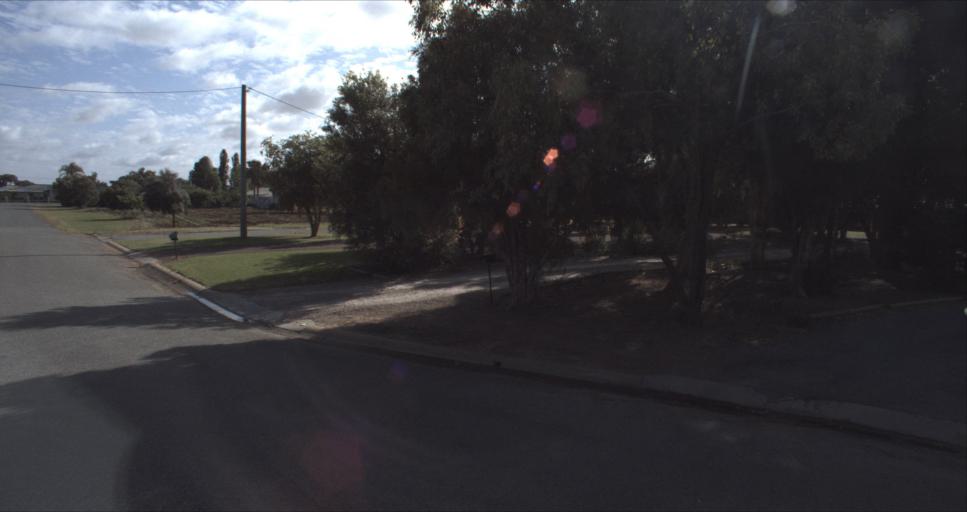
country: AU
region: New South Wales
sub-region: Leeton
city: Leeton
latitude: -34.5698
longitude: 146.3918
